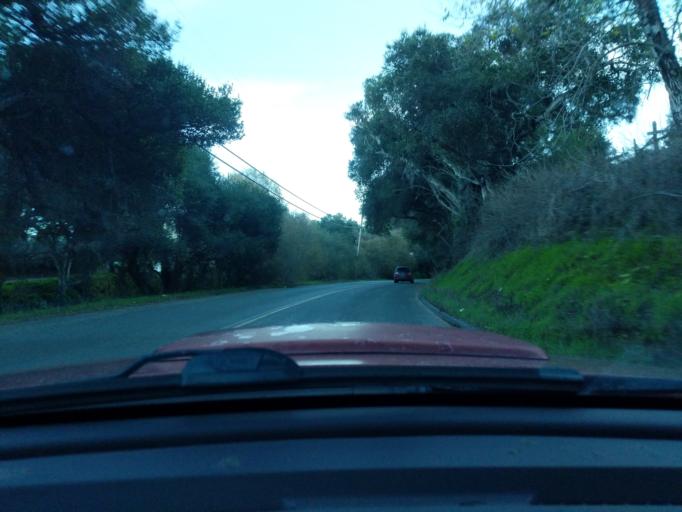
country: US
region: California
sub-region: San Benito County
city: Aromas
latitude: 36.8529
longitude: -121.6808
